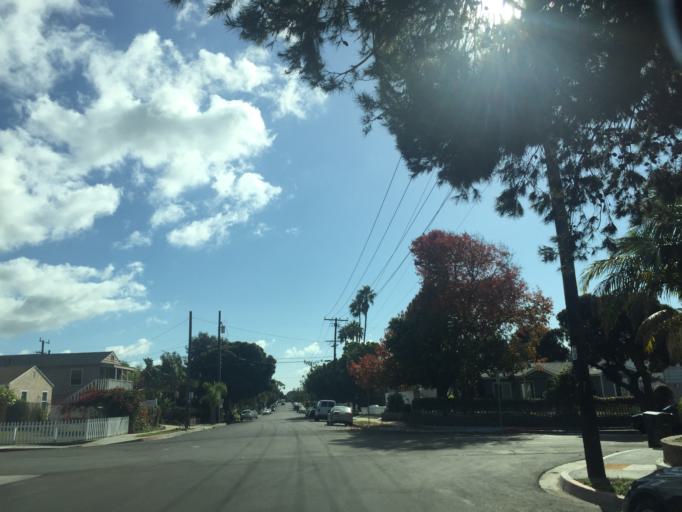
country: US
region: California
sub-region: San Diego County
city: La Jolla
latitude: 32.7967
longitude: -117.2419
